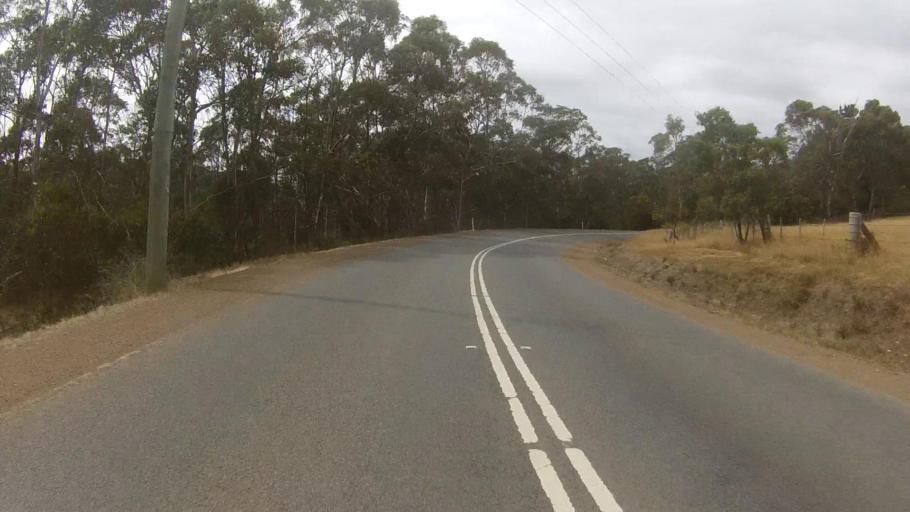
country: AU
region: Tasmania
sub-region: Kingborough
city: Margate
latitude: -42.9985
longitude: 147.2294
